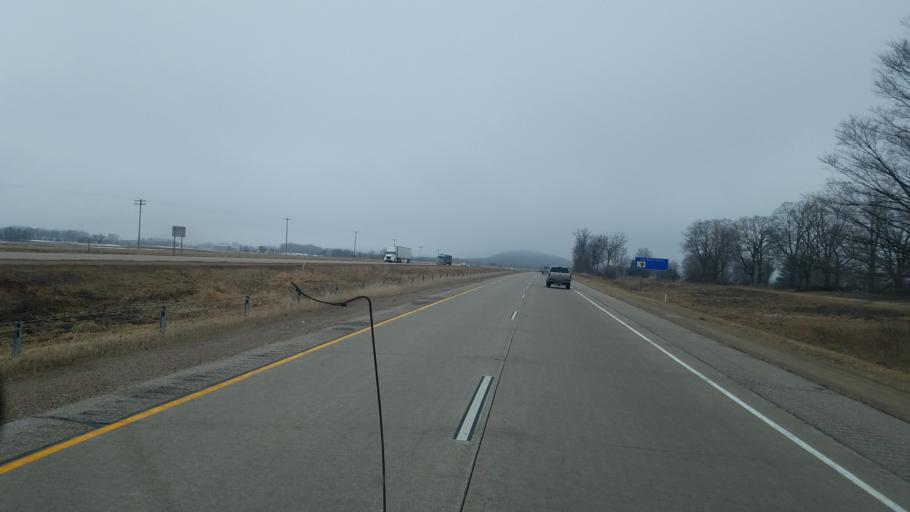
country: US
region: Wisconsin
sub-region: Waupaca County
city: Waupaca
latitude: 44.3296
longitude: -89.0285
